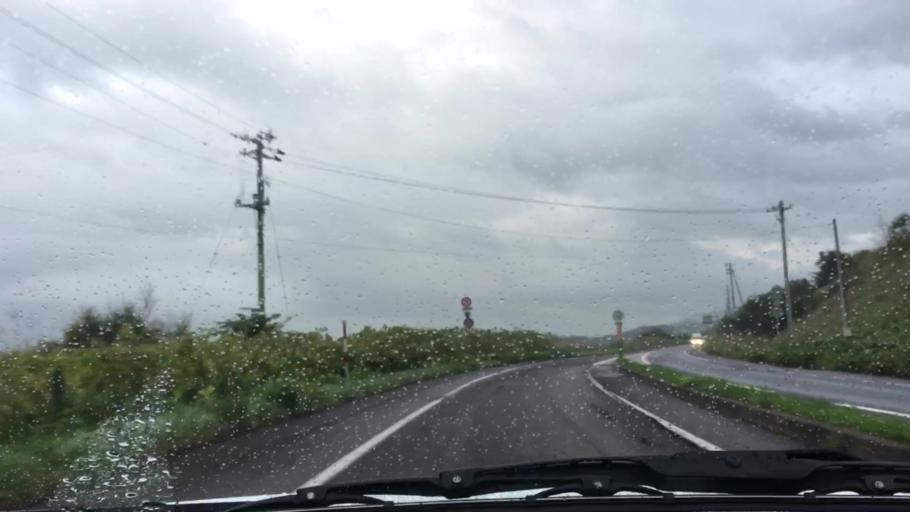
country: JP
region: Hokkaido
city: Nanae
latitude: 42.1871
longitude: 140.4357
